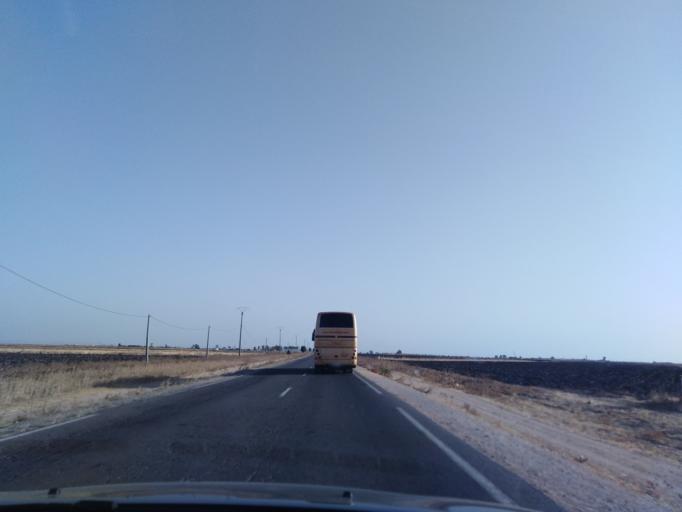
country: MA
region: Doukkala-Abda
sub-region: Safi
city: Youssoufia
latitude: 32.4842
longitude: -8.7680
